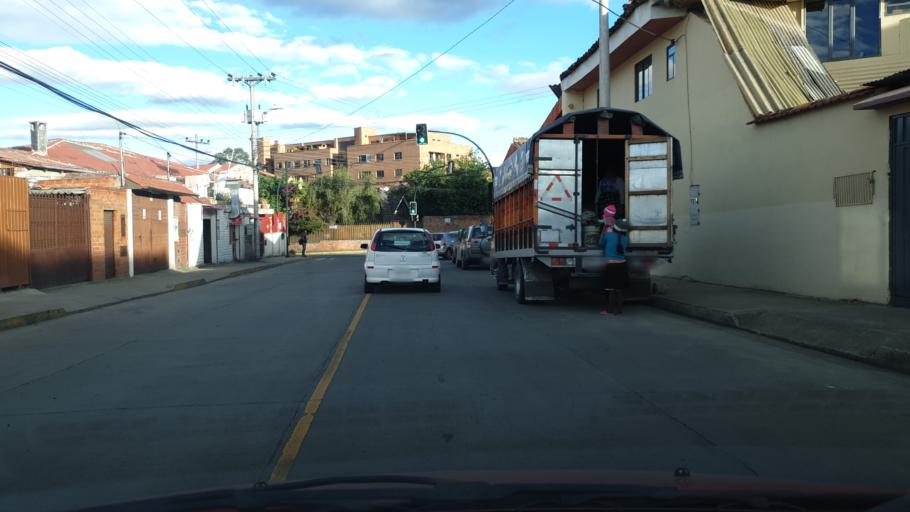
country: EC
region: Azuay
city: Cuenca
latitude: -2.9123
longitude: -79.0155
